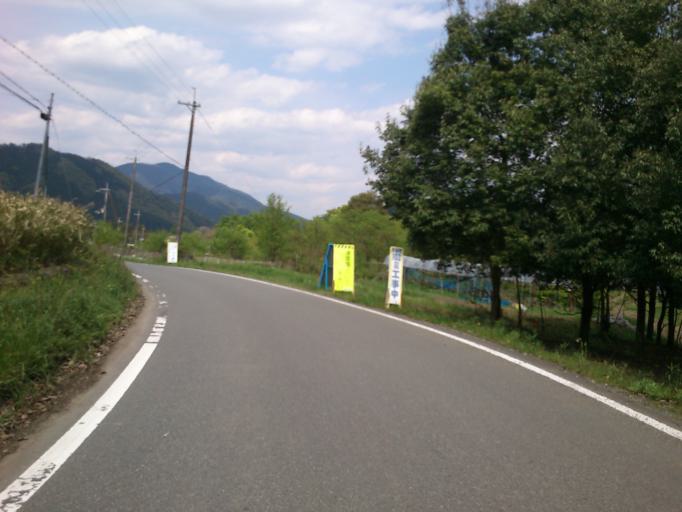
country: JP
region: Kyoto
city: Fukuchiyama
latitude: 35.3350
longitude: 134.9338
